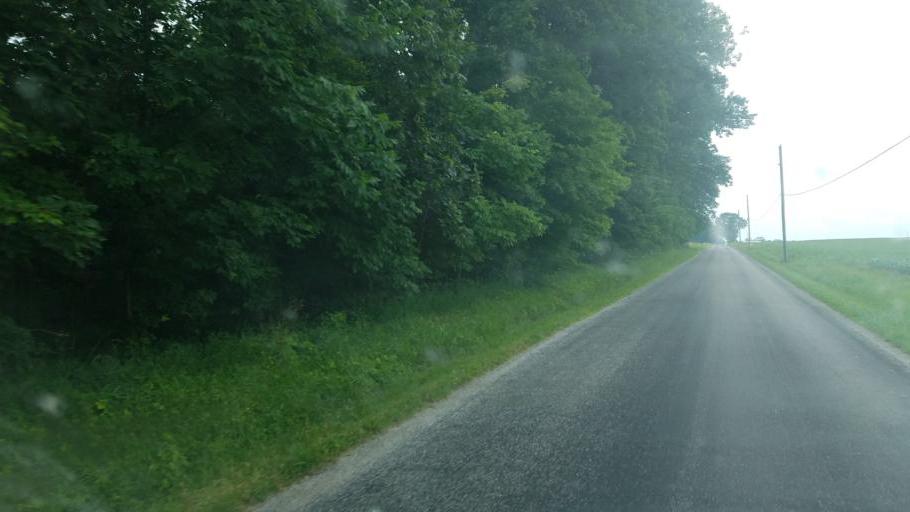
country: US
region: Ohio
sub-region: Wayne County
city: Apple Creek
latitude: 40.7776
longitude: -81.8327
